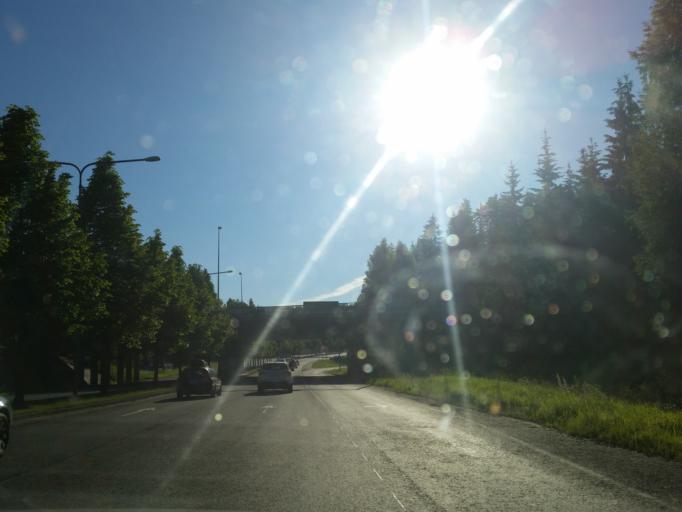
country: FI
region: Northern Savo
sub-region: Kuopio
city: Kuopio
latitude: 62.8845
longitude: 27.6378
